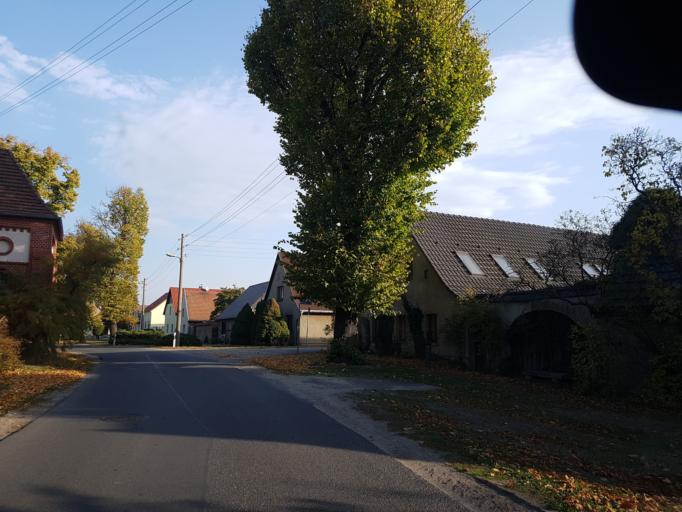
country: DE
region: Brandenburg
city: Finsterwalde
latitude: 51.6036
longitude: 13.6703
